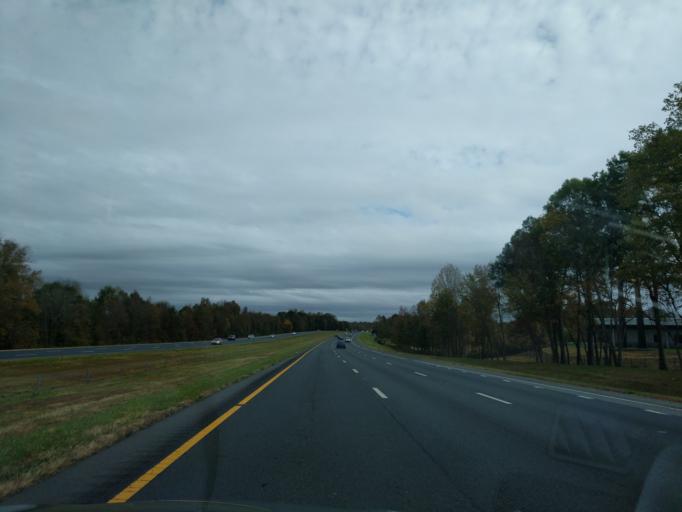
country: US
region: North Carolina
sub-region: Davidson County
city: Tyro
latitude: 35.7753
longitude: -80.3084
